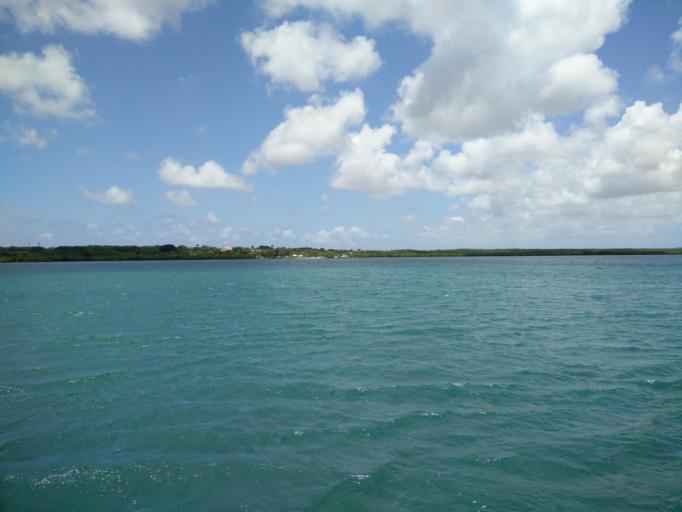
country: GP
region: Guadeloupe
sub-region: Guadeloupe
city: Petit-Canal
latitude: 16.3801
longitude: -61.5039
